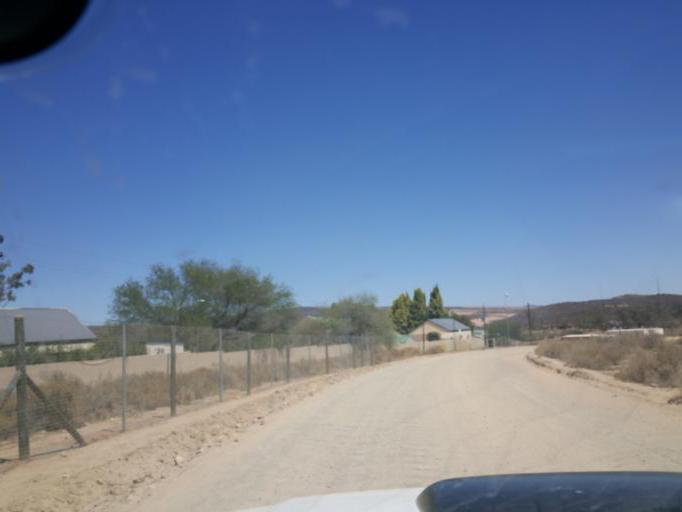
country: ZA
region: Western Cape
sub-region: West Coast District Municipality
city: Clanwilliam
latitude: -32.1943
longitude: 18.8907
